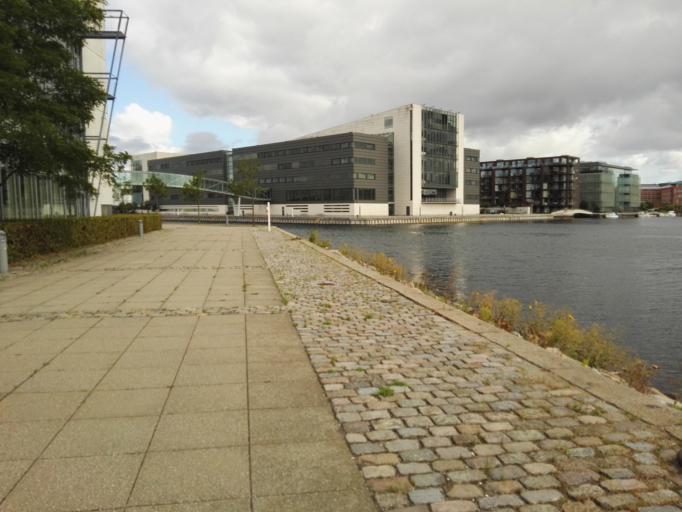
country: DK
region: Capital Region
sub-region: Frederiksberg Kommune
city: Frederiksberg
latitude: 55.6489
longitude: 12.5436
